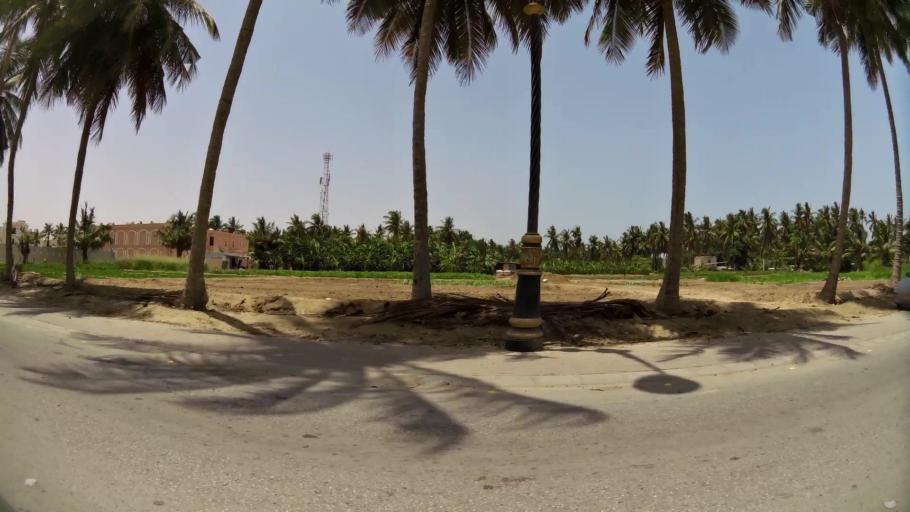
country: OM
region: Zufar
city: Salalah
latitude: 17.0122
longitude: 54.1099
